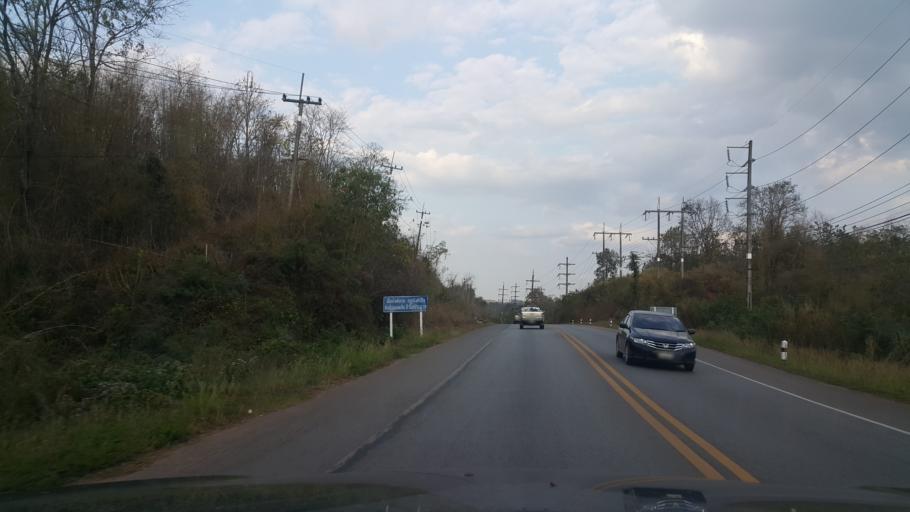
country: TH
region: Loei
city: Dan Sai
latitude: 17.3151
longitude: 101.2110
